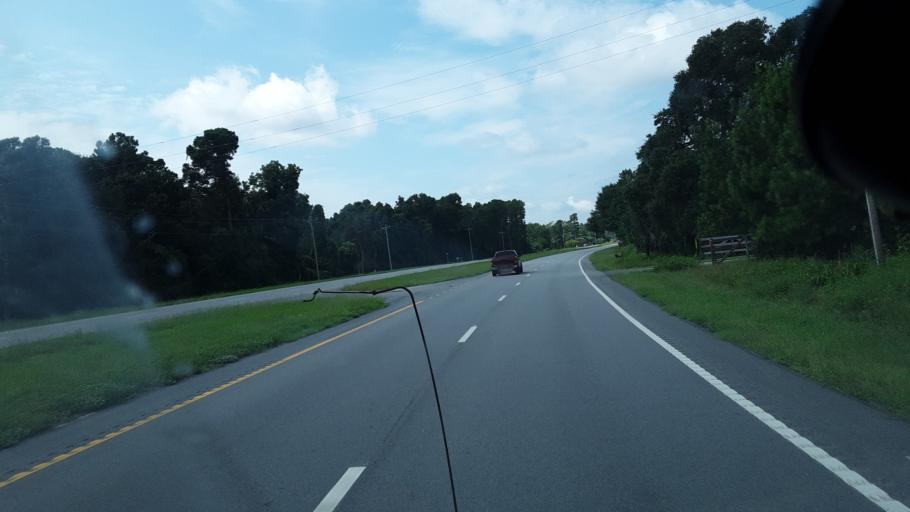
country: US
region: South Carolina
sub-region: Charleston County
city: Awendaw
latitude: 33.0557
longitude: -79.5467
